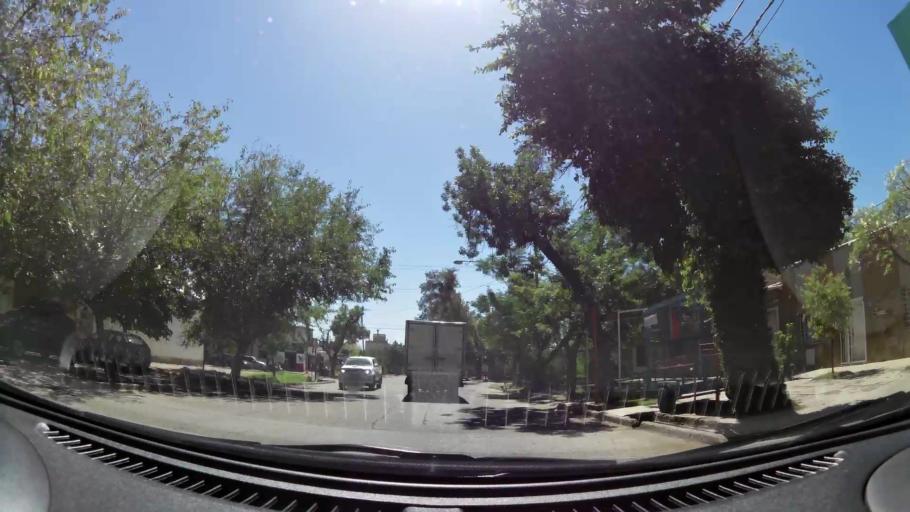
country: AR
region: Mendoza
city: Mendoza
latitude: -32.8805
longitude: -68.8134
